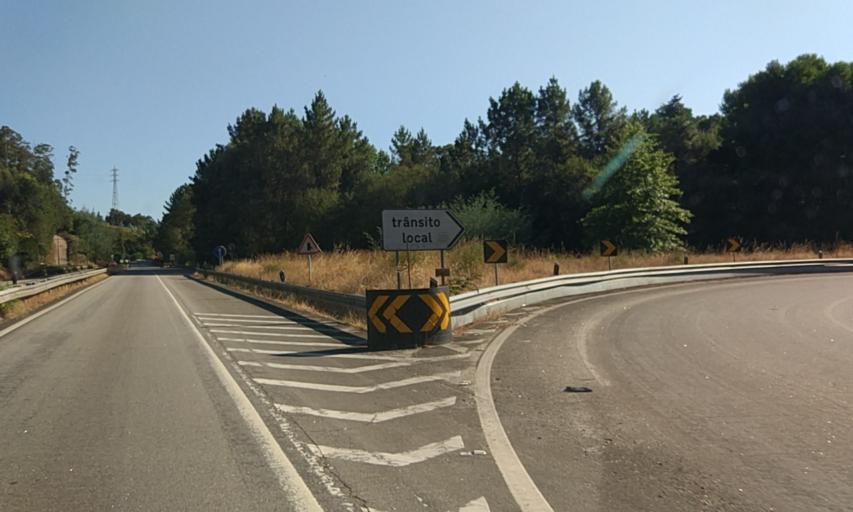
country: PT
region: Porto
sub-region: Santo Tirso
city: Sao Miguel do Couto
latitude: 41.3154
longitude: -8.4699
